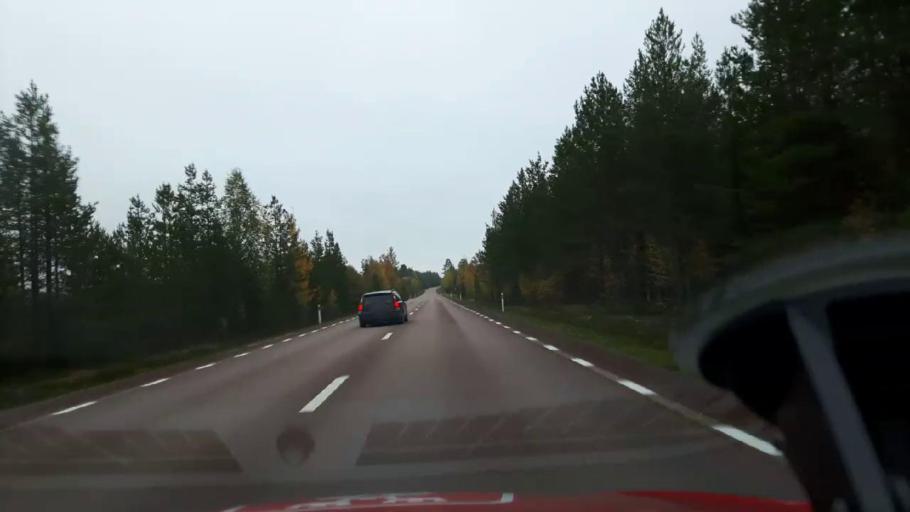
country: SE
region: Jaemtland
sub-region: Bergs Kommun
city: Hoverberg
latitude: 62.4536
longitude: 14.5537
